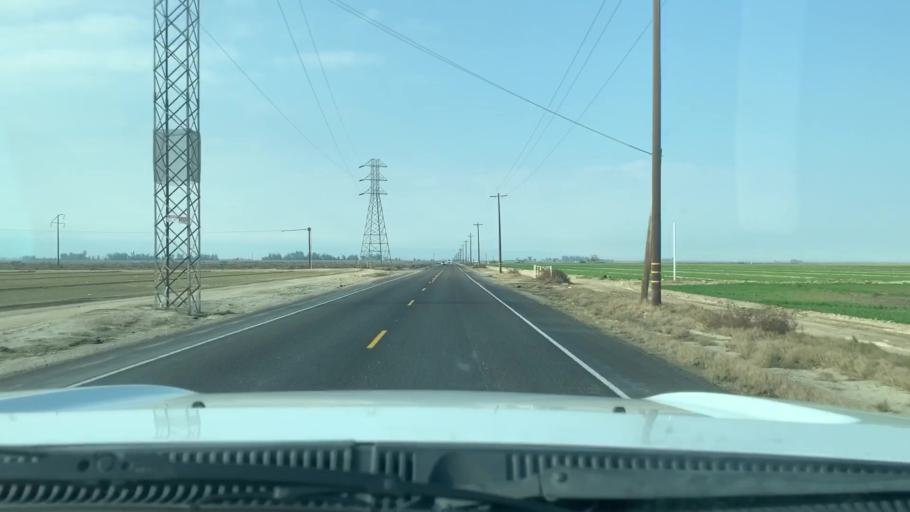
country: US
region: California
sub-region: Kern County
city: Buttonwillow
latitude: 35.4421
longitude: -119.3744
